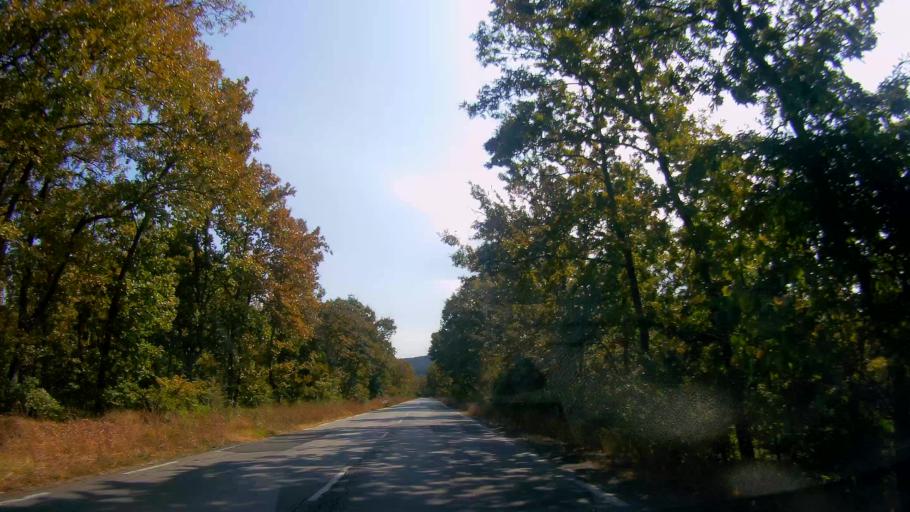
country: BG
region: Burgas
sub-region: Obshtina Sungurlare
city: Sungurlare
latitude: 42.8103
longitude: 26.8827
